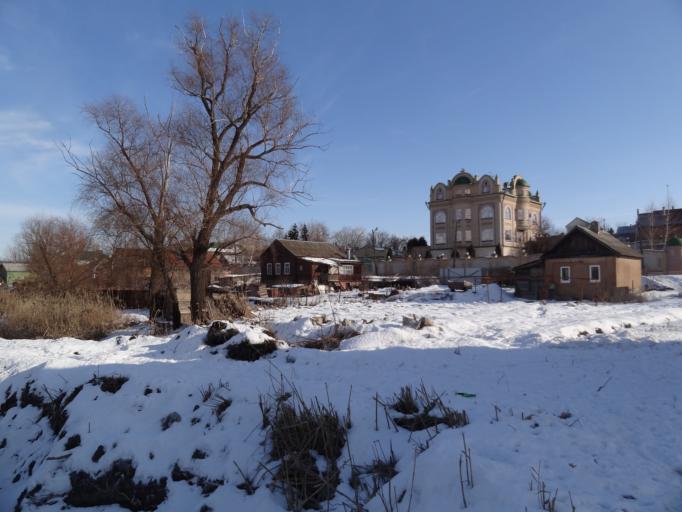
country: RU
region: Saratov
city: Engel's
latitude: 51.4778
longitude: 46.1116
